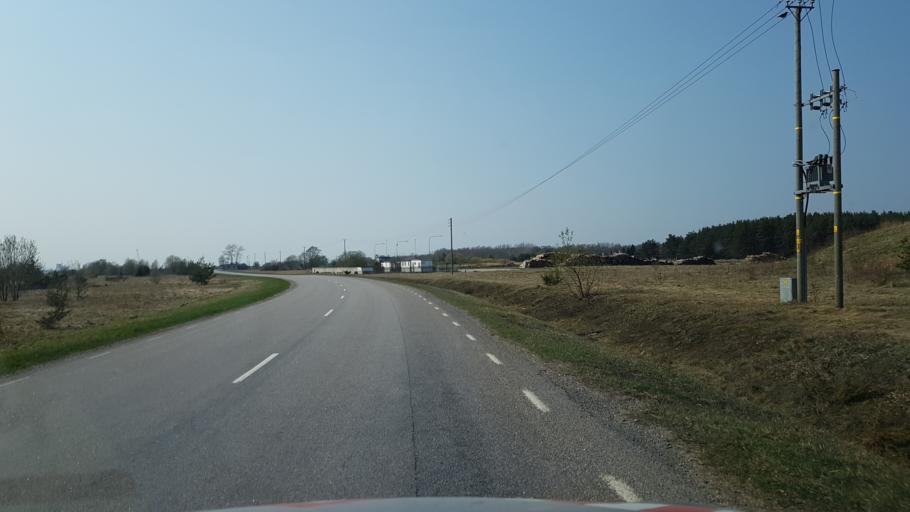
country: EE
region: Harju
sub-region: Paldiski linn
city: Paldiski
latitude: 59.3273
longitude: 24.1177
